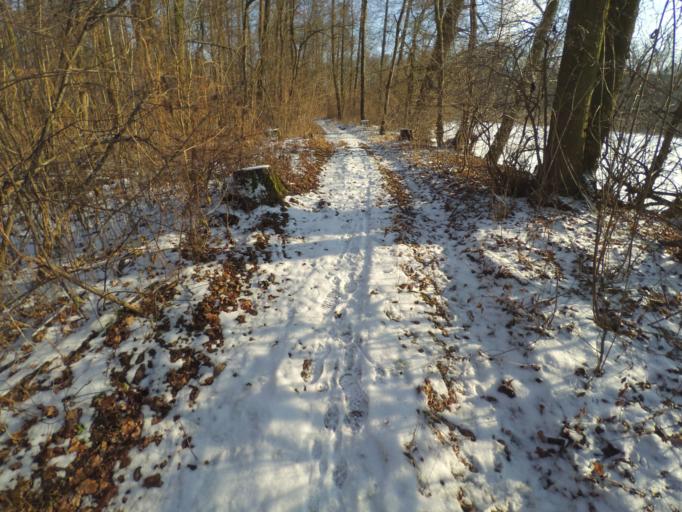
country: CZ
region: Central Bohemia
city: Libis
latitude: 50.2867
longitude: 14.5147
